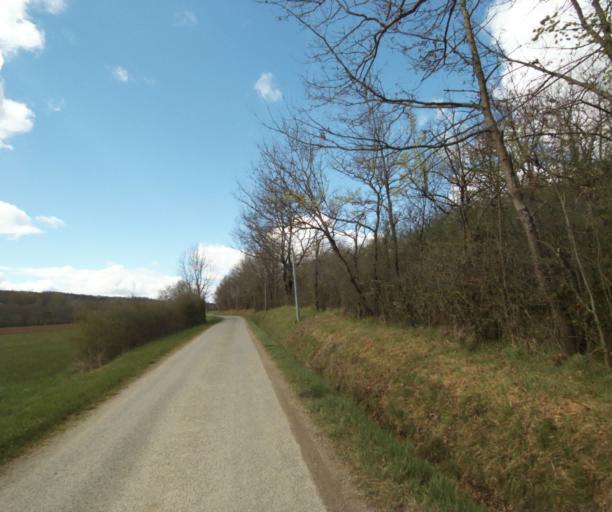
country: FR
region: Midi-Pyrenees
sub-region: Departement de l'Ariege
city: Saverdun
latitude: 43.1909
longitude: 1.5634
